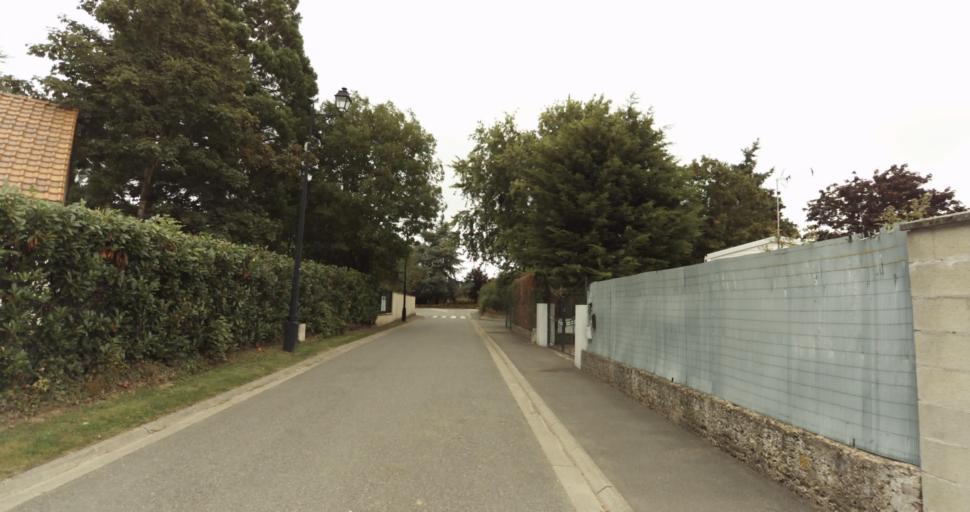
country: FR
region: Haute-Normandie
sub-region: Departement de l'Eure
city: Gravigny
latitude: 49.0372
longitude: 1.2092
